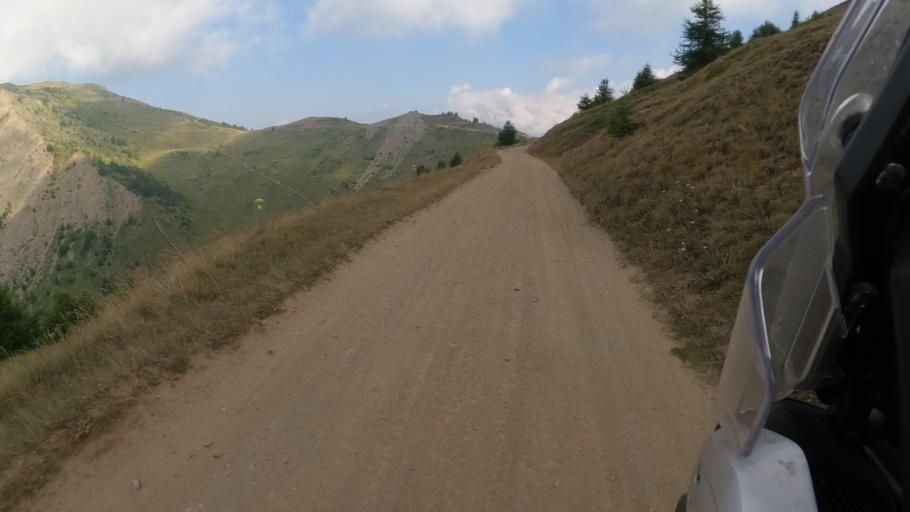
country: IT
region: Piedmont
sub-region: Provincia di Torino
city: Pragelato-Rua
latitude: 45.0346
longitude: 6.9197
